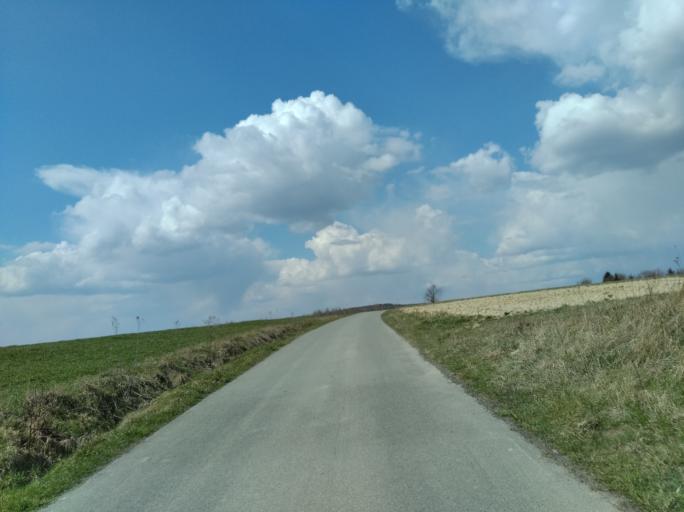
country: PL
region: Subcarpathian Voivodeship
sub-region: Powiat ropczycko-sedziszowski
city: Zagorzyce
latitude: 49.9364
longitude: 21.7180
